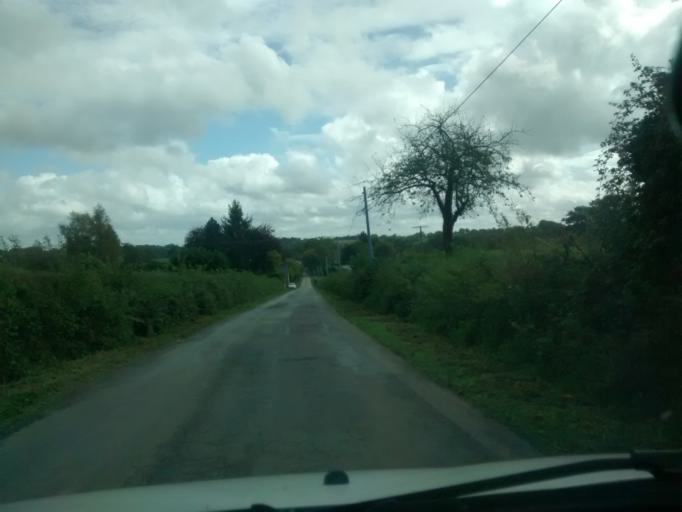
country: FR
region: Brittany
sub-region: Departement d'Ille-et-Vilaine
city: Chateaubourg
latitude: 48.1285
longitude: -1.4023
